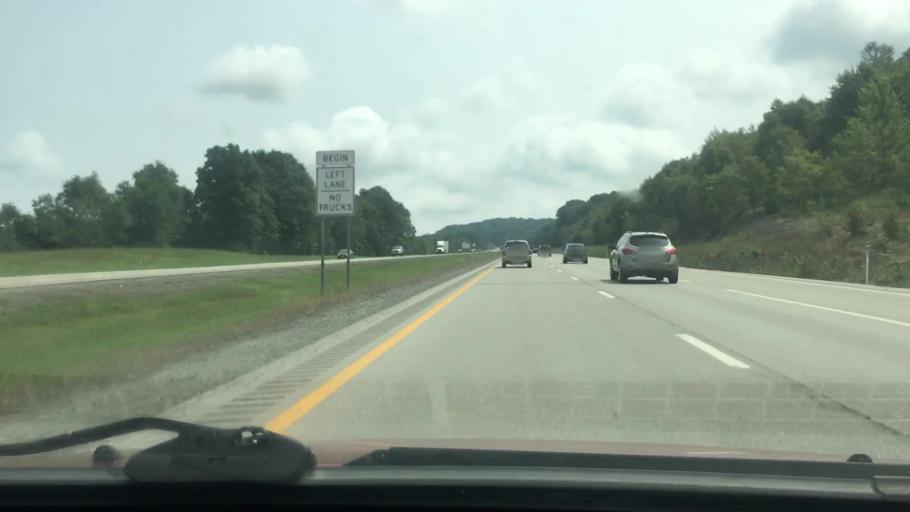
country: US
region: West Virginia
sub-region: Preston County
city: Terra Alta
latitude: 39.6574
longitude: -79.5270
